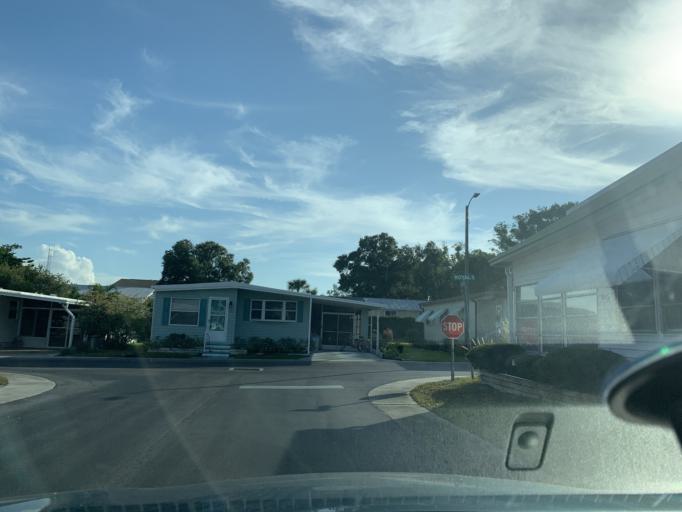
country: US
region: Florida
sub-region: Pinellas County
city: Ridgecrest
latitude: 27.8991
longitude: -82.7943
